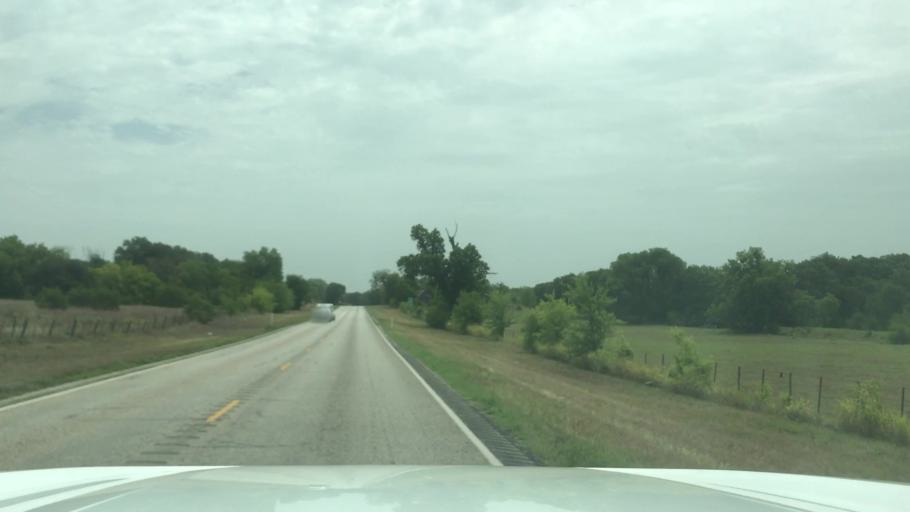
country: US
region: Texas
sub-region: Hamilton County
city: Hico
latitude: 32.0413
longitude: -98.1297
